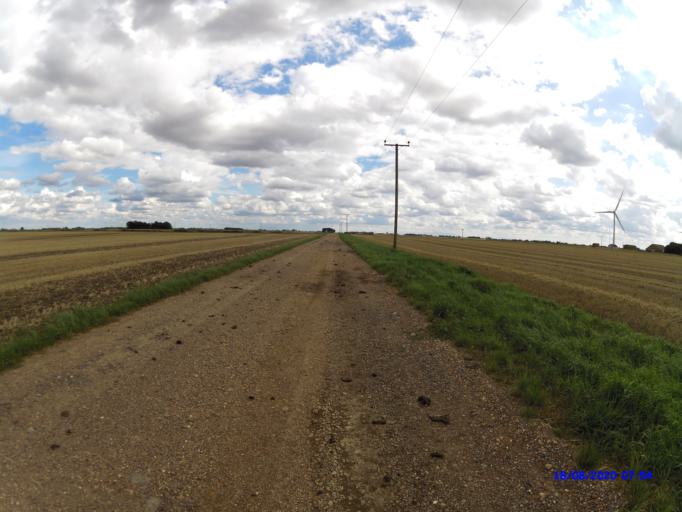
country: GB
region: England
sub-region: Cambridgeshire
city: Whittlesey
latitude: 52.5168
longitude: -0.0893
